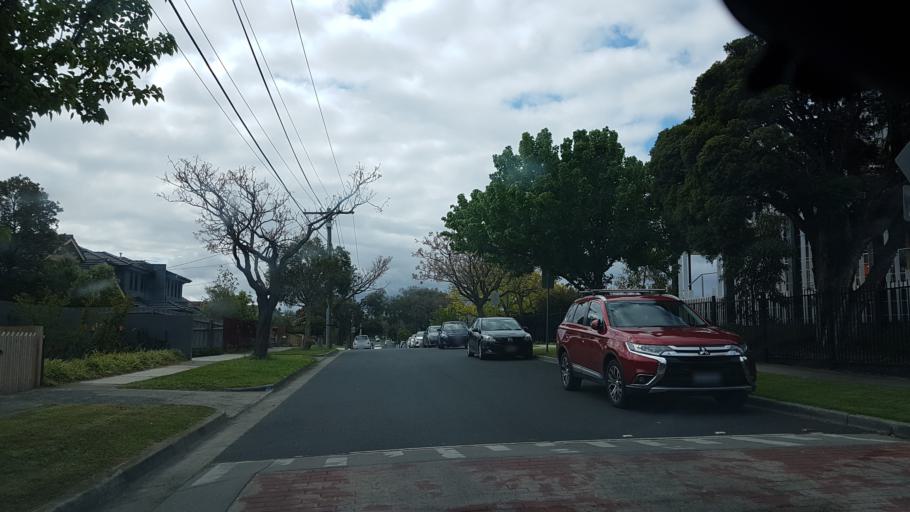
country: AU
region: Victoria
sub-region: Glen Eira
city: Bentleigh
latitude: -37.9248
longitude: 145.0394
